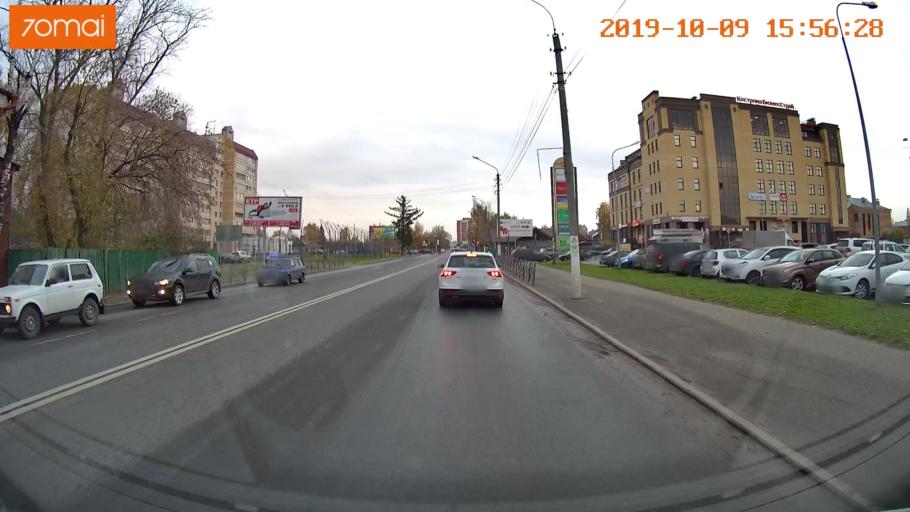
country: RU
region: Kostroma
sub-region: Kostromskoy Rayon
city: Kostroma
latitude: 57.7746
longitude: 40.9456
